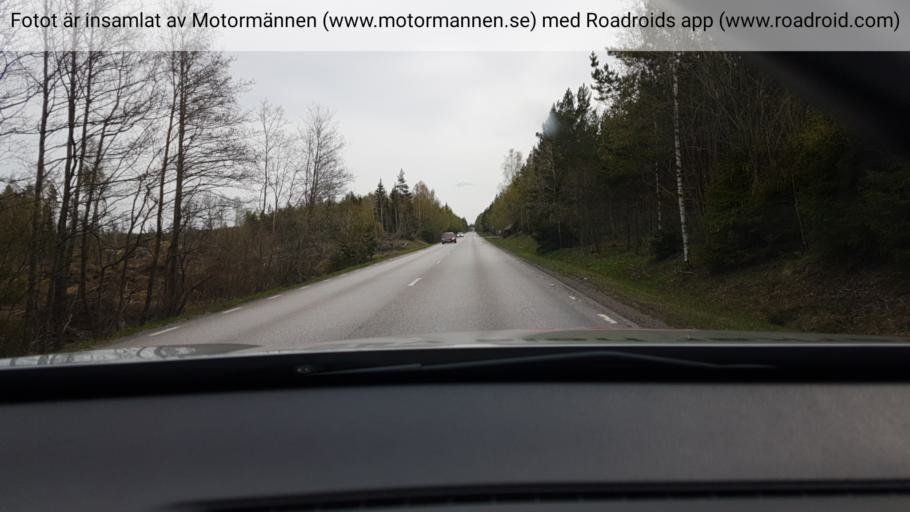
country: SE
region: Stockholm
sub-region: Norrtalje Kommun
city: Nykvarn
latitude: 59.8205
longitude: 18.0449
